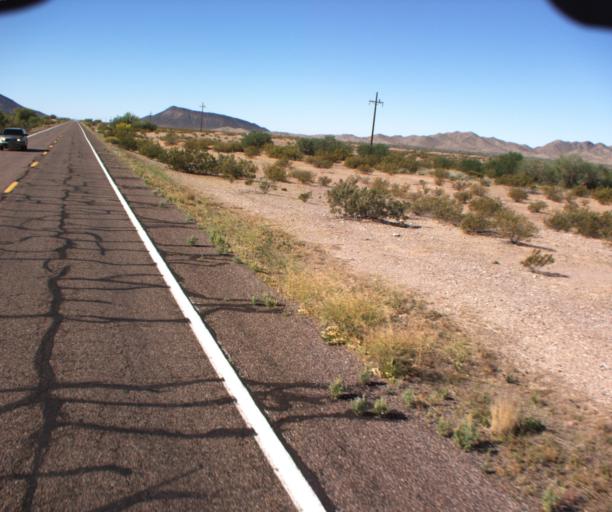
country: US
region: Arizona
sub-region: Maricopa County
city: Gila Bend
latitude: 32.8039
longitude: -112.7974
